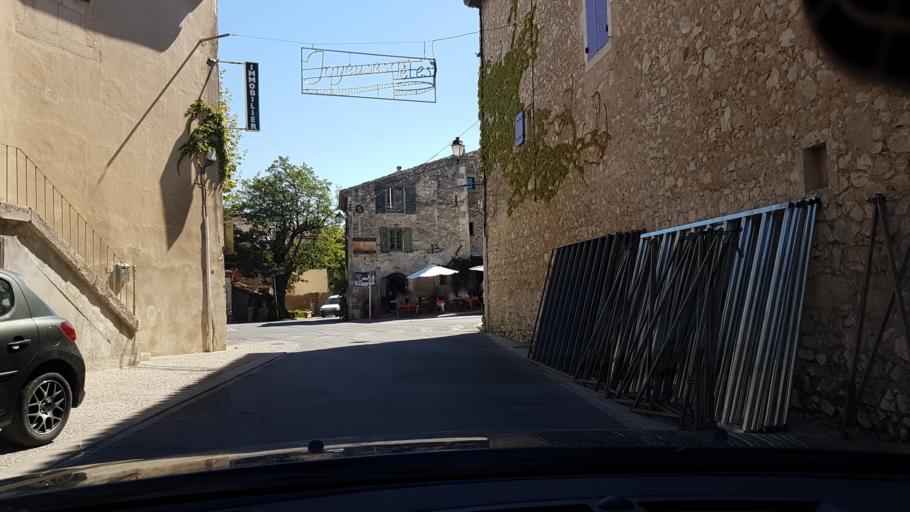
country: FR
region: Provence-Alpes-Cote d'Azur
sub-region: Departement des Bouches-du-Rhone
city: Eygalieres
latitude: 43.7607
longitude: 4.9497
